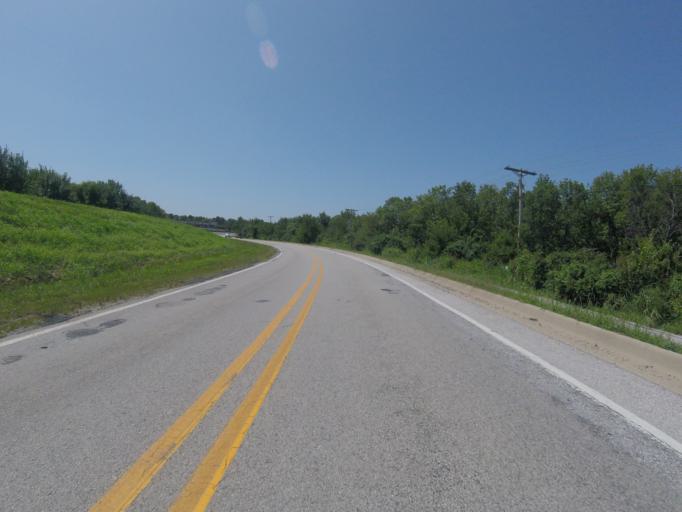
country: US
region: Arkansas
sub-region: Washington County
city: Johnson
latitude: 36.1059
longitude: -94.1827
